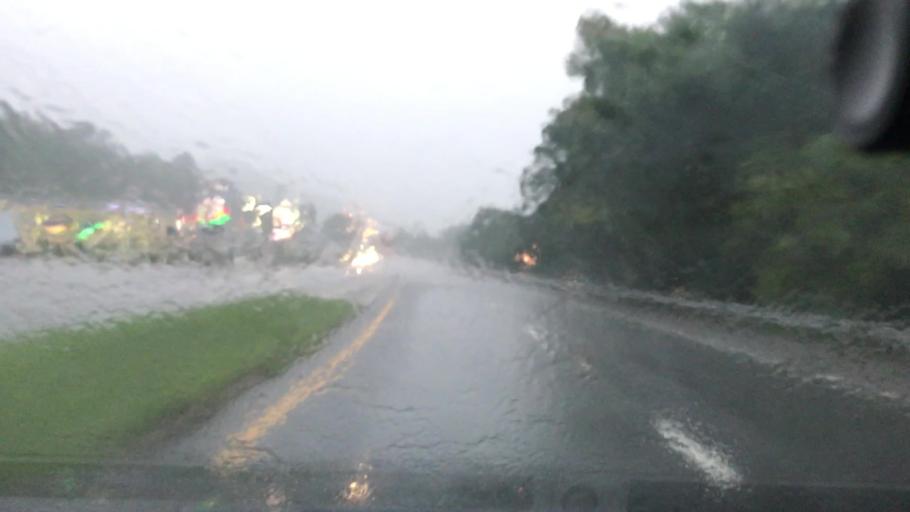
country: US
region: Virginia
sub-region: Giles County
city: Narrows
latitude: 37.3356
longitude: -80.7997
